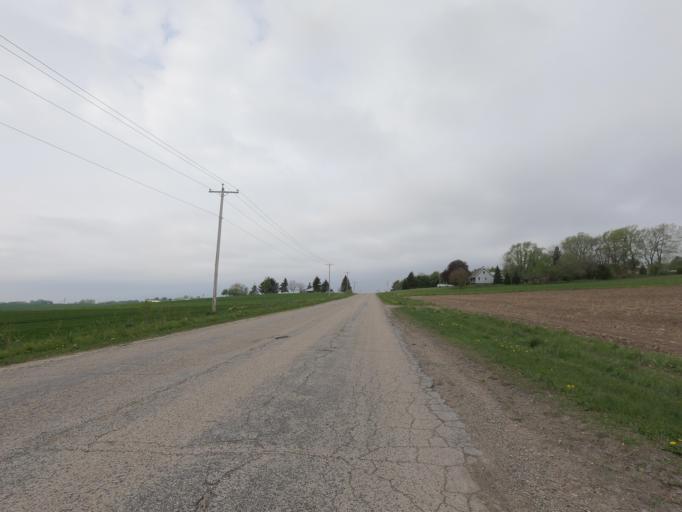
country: US
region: Wisconsin
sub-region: Jefferson County
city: Jefferson
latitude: 43.0319
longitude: -88.7798
